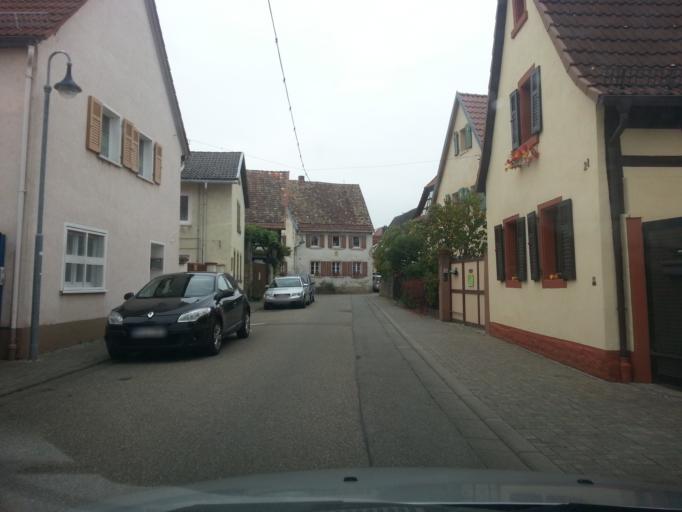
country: DE
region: Rheinland-Pfalz
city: Lachen-Speyerdorf
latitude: 49.3211
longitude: 8.1982
